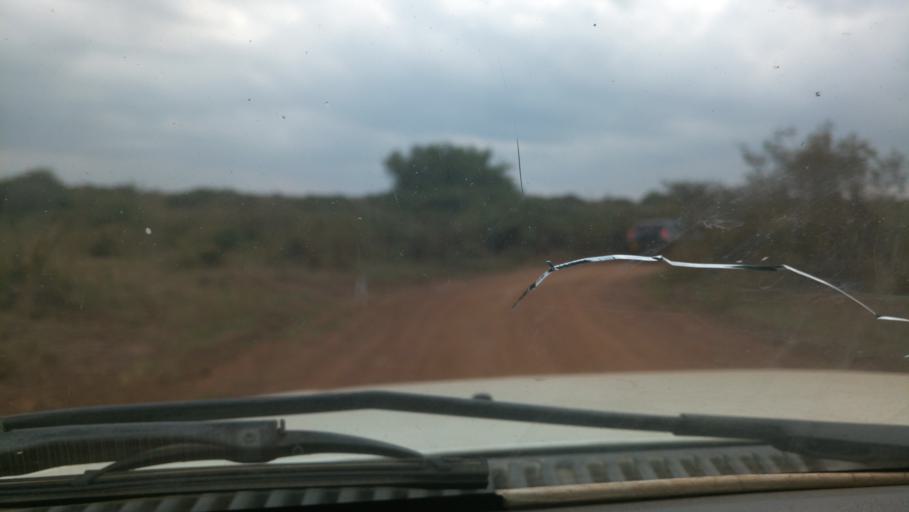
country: KE
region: Nairobi Area
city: Nairobi
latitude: -1.3619
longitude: 36.8329
